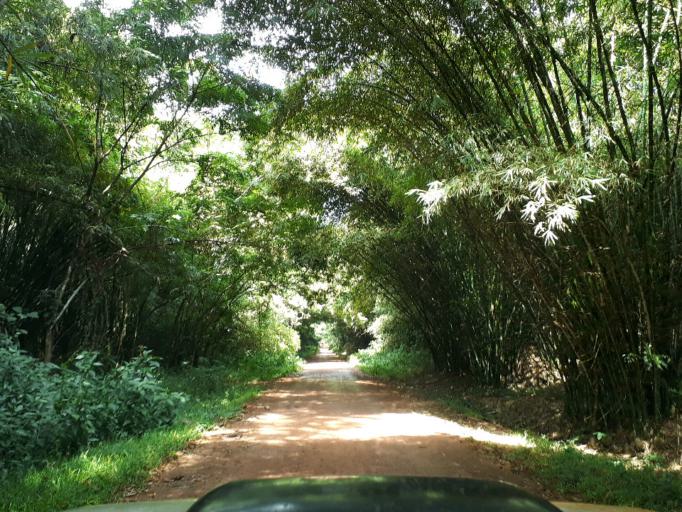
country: CD
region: Eastern Province
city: Buta
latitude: 2.8771
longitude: 24.4573
